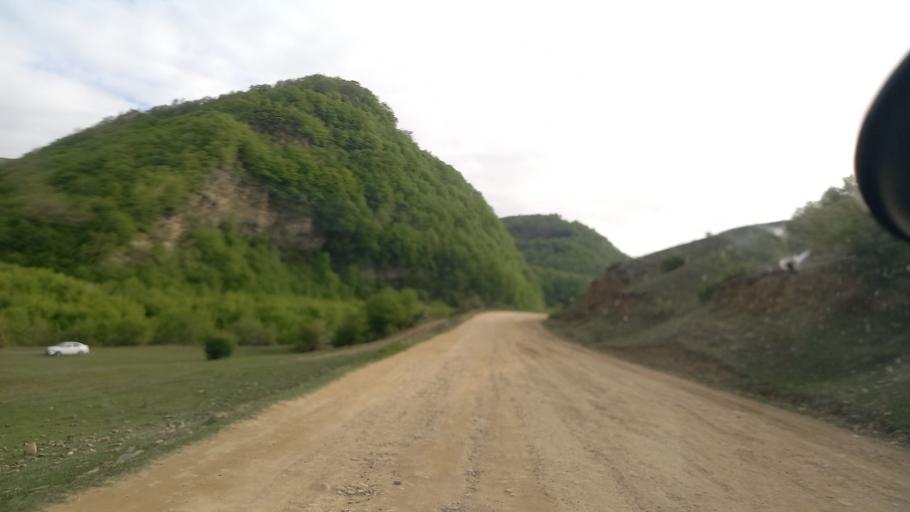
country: RU
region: Dagestan
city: Khuchni
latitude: 41.9625
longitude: 47.8689
